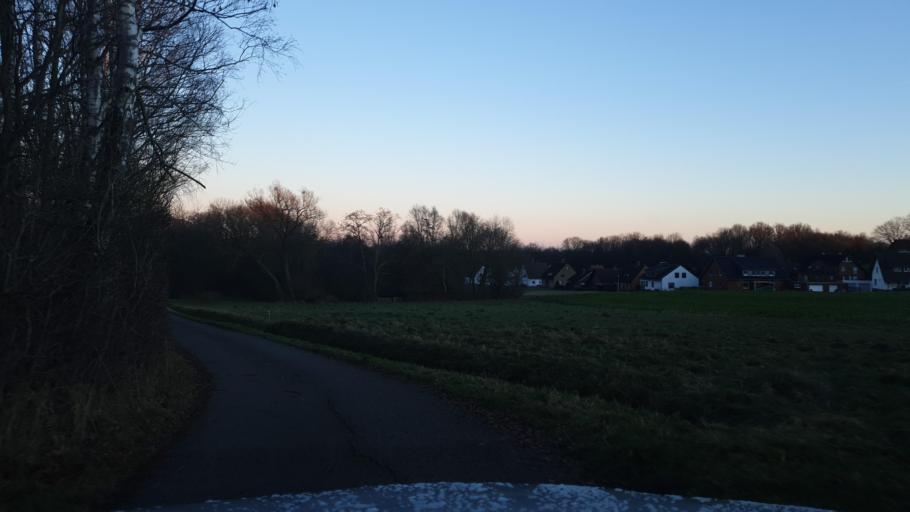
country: DE
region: North Rhine-Westphalia
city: Bad Oeynhausen
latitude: 52.2390
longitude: 8.8227
